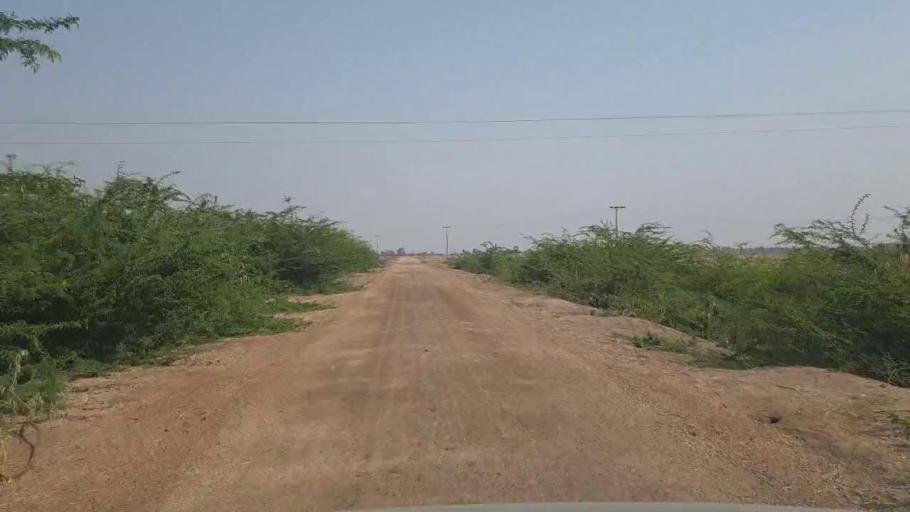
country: PK
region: Sindh
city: Chor
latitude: 25.4797
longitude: 69.7373
